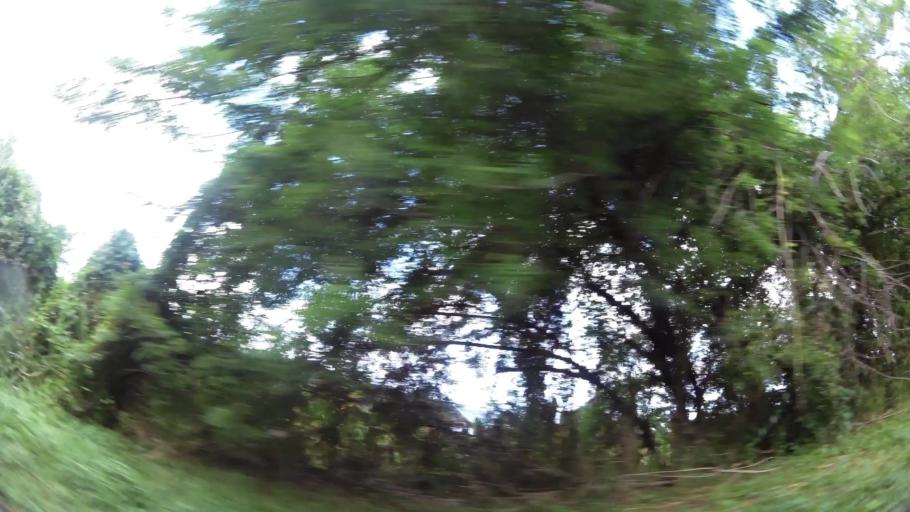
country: MQ
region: Martinique
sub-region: Martinique
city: Le Lorrain
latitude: 14.8276
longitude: -61.0362
